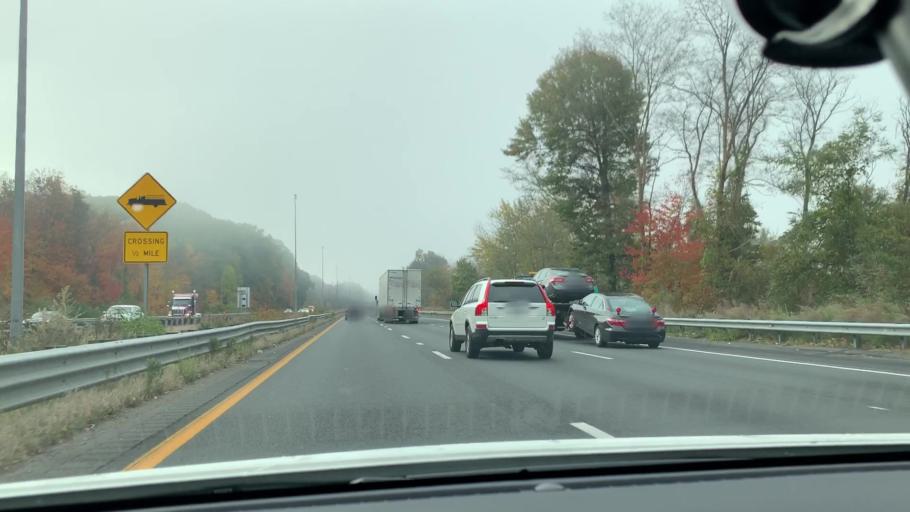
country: US
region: Massachusetts
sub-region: Hampden County
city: Longmeadow
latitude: 42.0425
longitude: -72.5888
